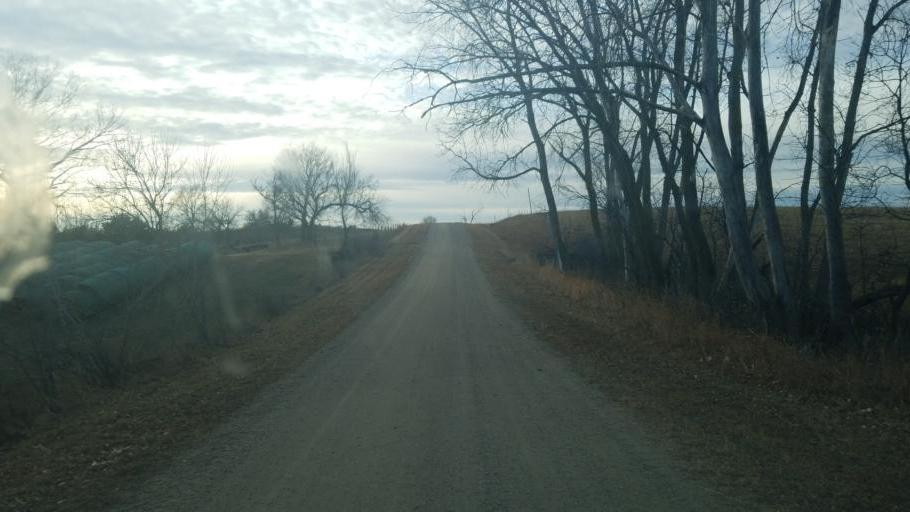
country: US
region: Nebraska
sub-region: Knox County
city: Center
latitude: 42.6980
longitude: -97.8413
